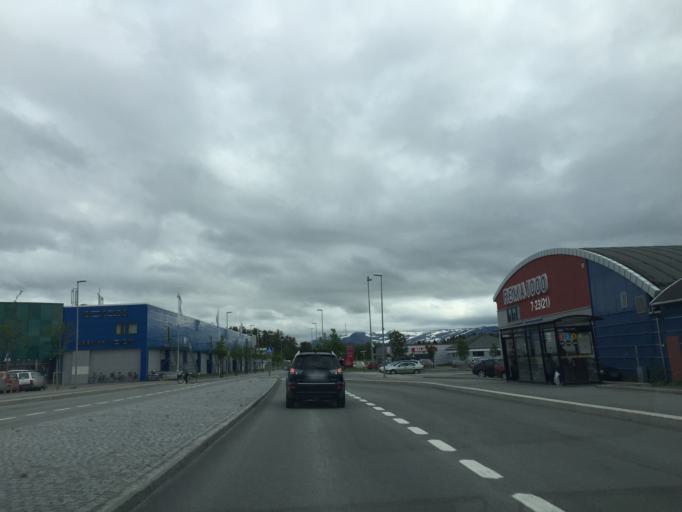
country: NO
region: Nordland
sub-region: Bodo
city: Bodo
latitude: 67.2773
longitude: 14.4199
